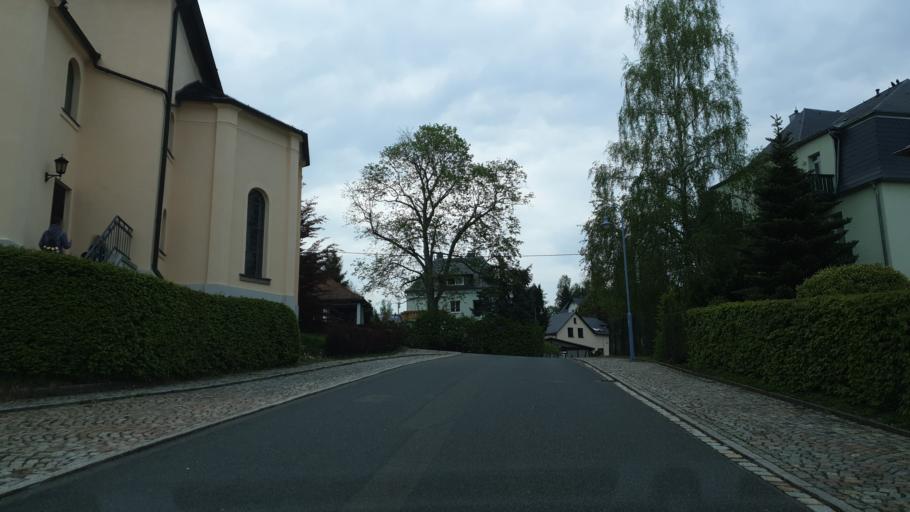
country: DE
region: Saxony
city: Oelsnitz
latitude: 50.7231
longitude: 12.6979
